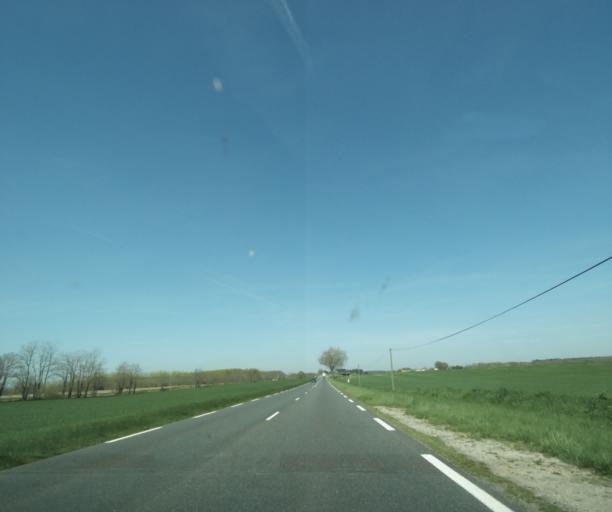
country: FR
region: Auvergne
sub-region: Departement de l'Allier
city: Trevol
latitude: 46.6698
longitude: 3.2383
